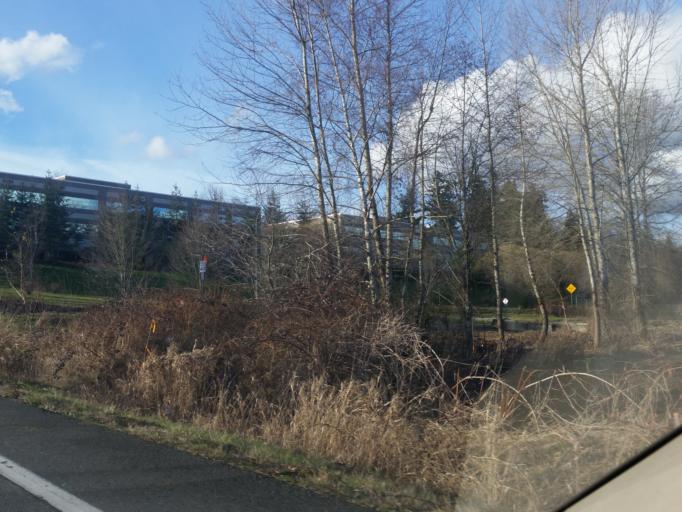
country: US
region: Washington
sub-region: King County
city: Kingsgate
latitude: 47.7043
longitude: -122.1527
